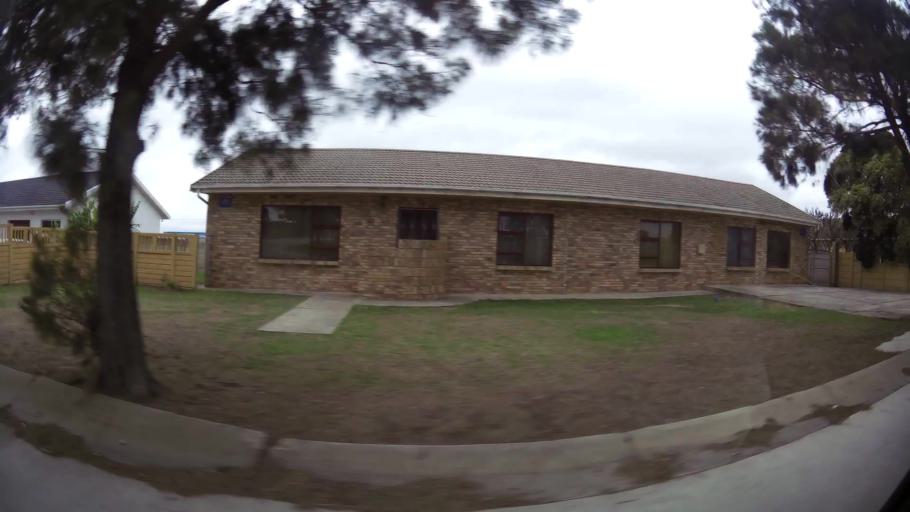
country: ZA
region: Eastern Cape
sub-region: Nelson Mandela Bay Metropolitan Municipality
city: Port Elizabeth
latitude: -33.9172
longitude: 25.5735
